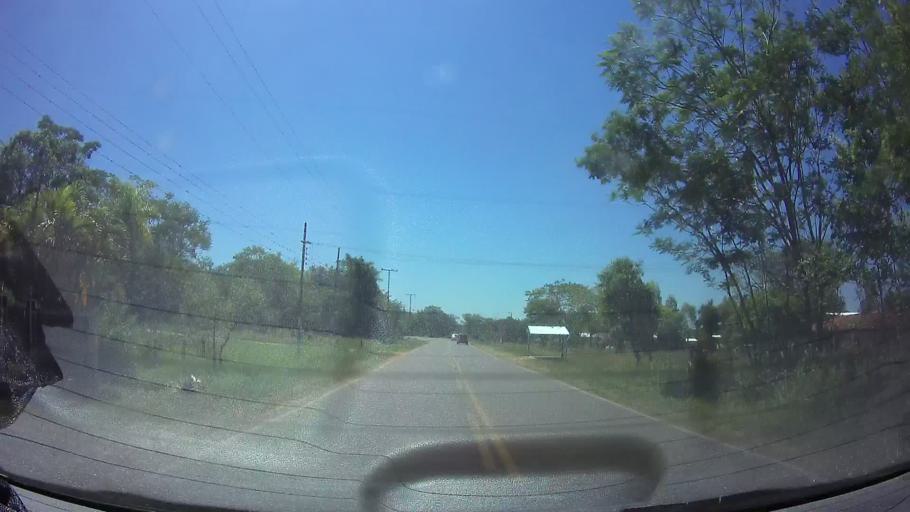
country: PY
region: Central
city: Aregua
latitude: -25.2637
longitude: -57.4169
